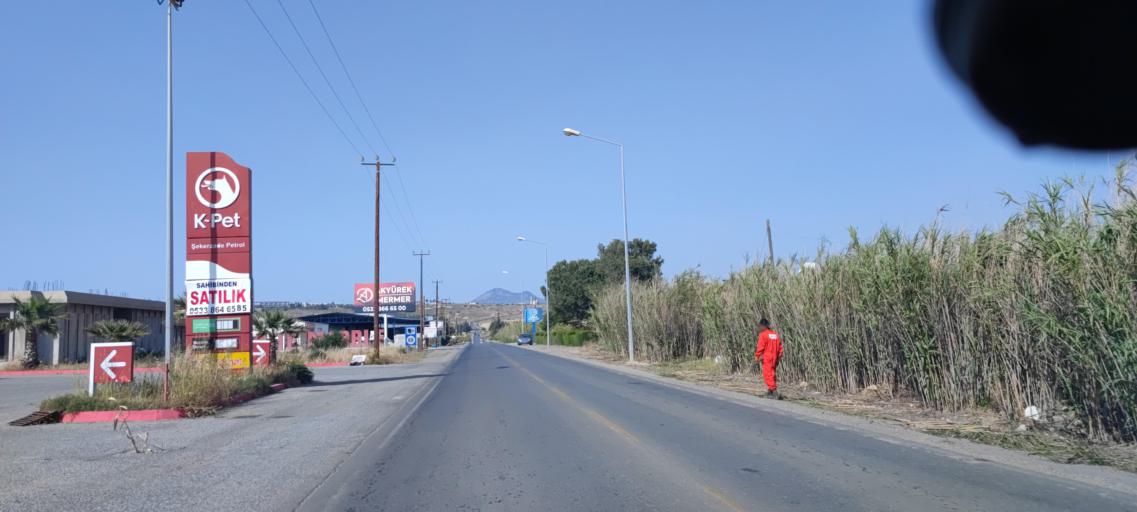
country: CY
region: Lefkosia
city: Morfou
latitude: 35.2336
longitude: 33.0186
